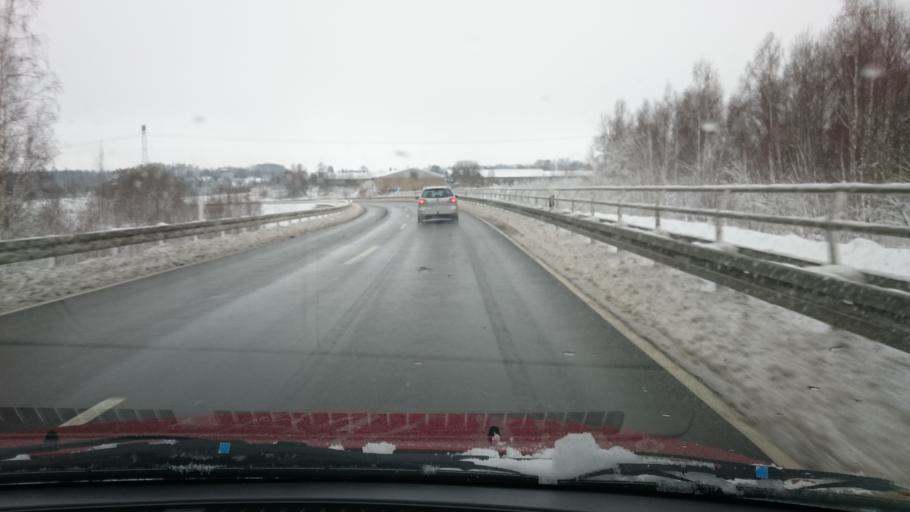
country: DE
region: Saxony
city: Mulsen
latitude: 50.7242
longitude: 12.5578
